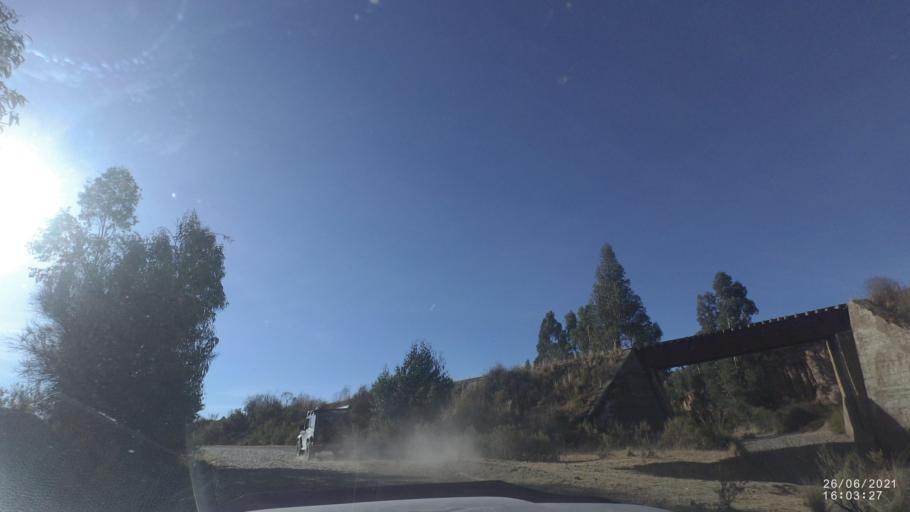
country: BO
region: Cochabamba
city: Arani
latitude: -17.8359
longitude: -65.7514
